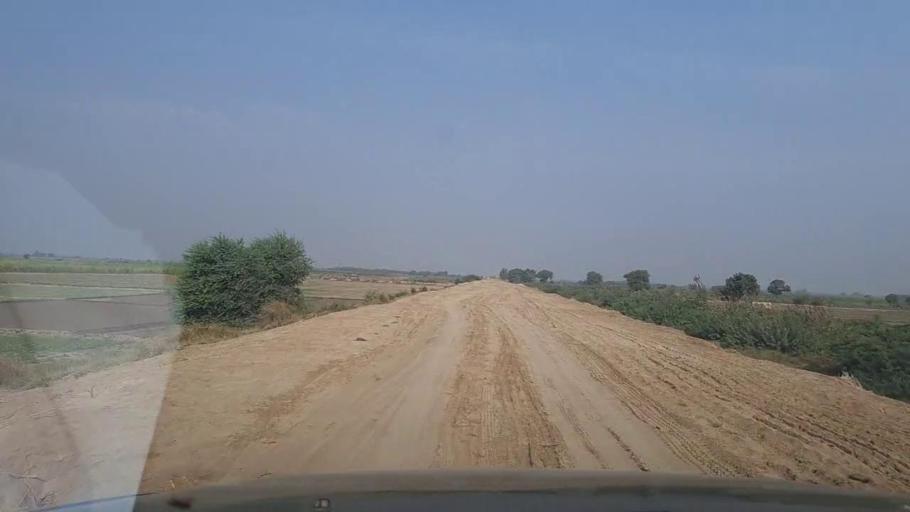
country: PK
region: Sindh
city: Bulri
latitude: 24.9934
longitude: 68.2916
